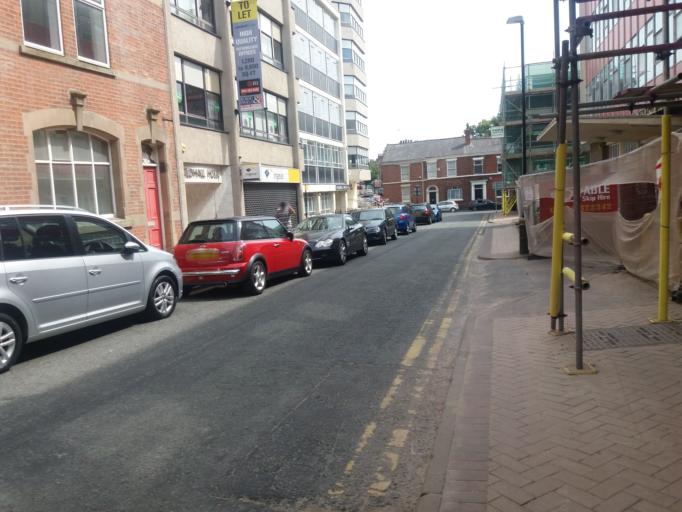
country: GB
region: England
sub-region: Lancashire
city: Preston
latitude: 53.7570
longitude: -2.7000
